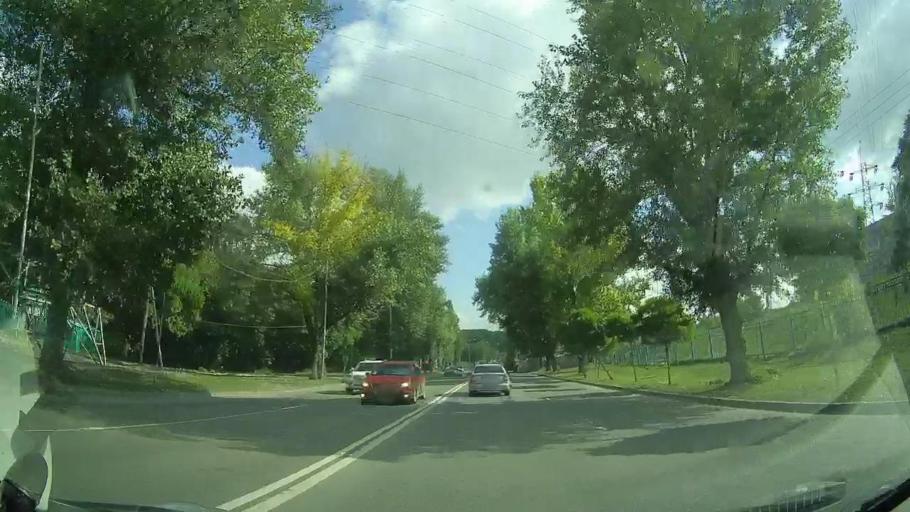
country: RU
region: Rostov
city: Imeni Chkalova
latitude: 47.2589
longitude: 39.7910
